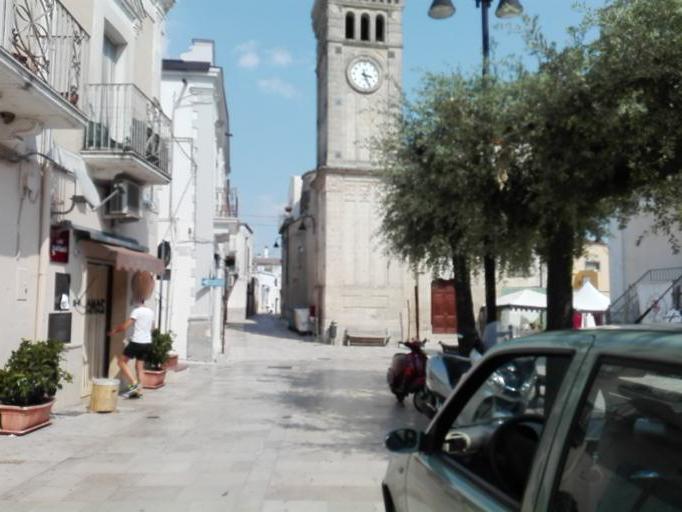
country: IT
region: Basilicate
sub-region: Provincia di Matera
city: Miglionico
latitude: 40.5696
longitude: 16.5005
